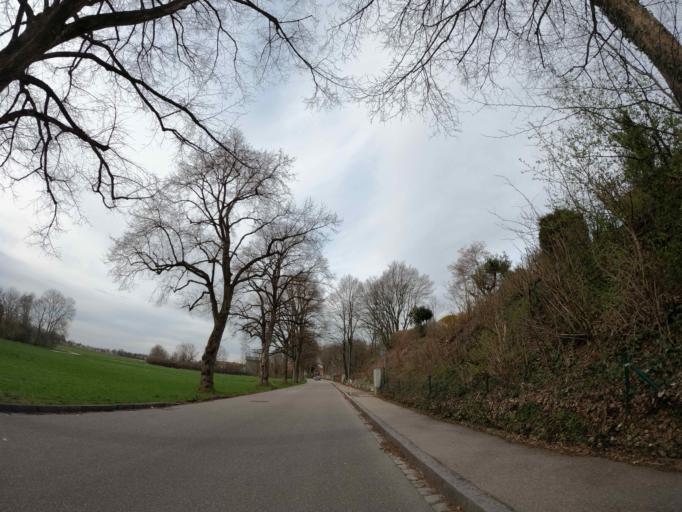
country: DE
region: Bavaria
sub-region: Upper Bavaria
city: Taufkirchen
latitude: 48.0453
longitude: 11.6235
